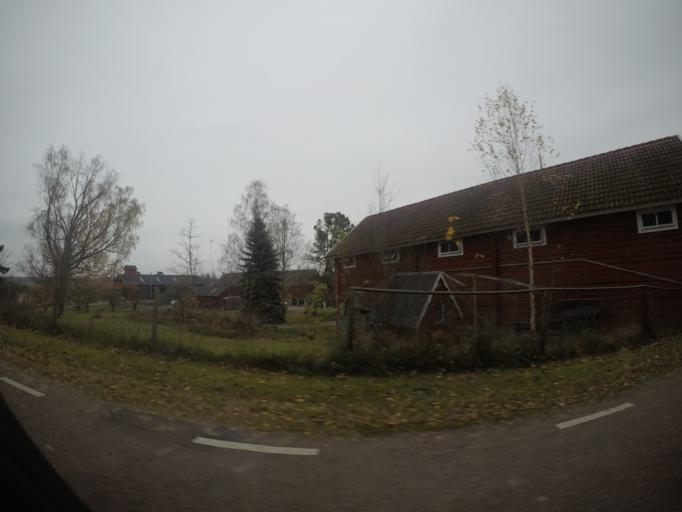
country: SE
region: Vaestmanland
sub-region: Kopings Kommun
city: Koping
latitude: 59.5473
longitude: 16.1084
